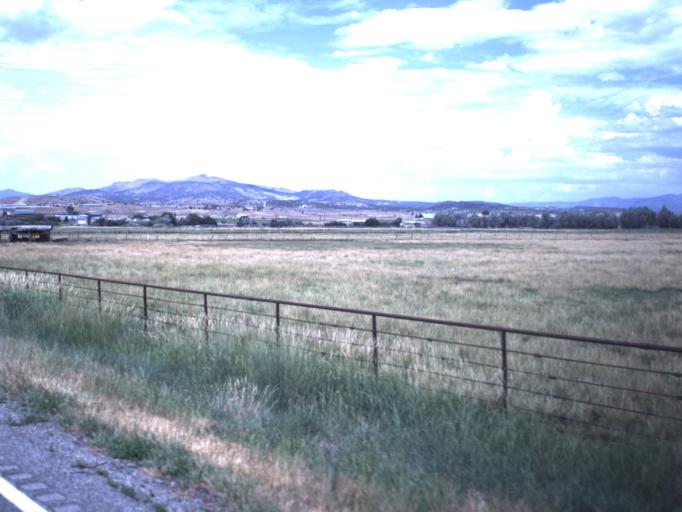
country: US
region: Utah
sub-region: Sanpete County
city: Moroni
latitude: 39.5131
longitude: -111.5712
